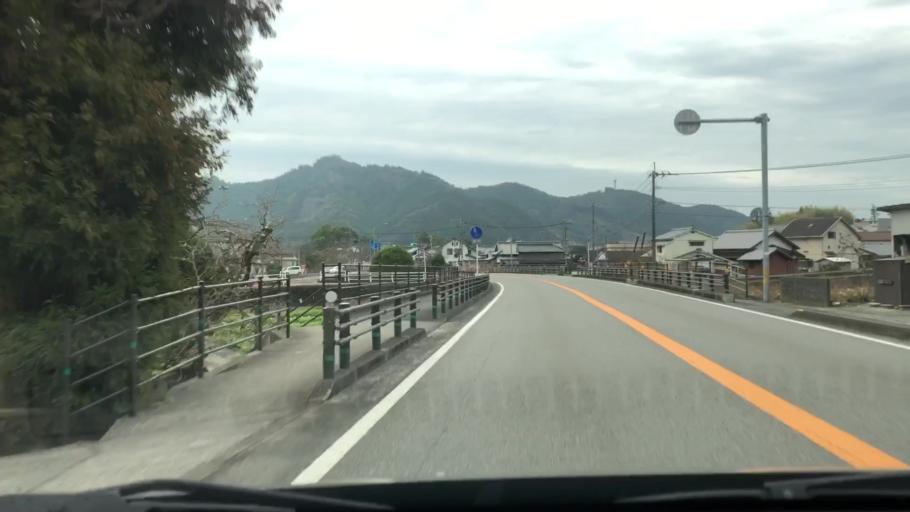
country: JP
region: Oita
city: Saiki
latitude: 32.9839
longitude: 131.8479
